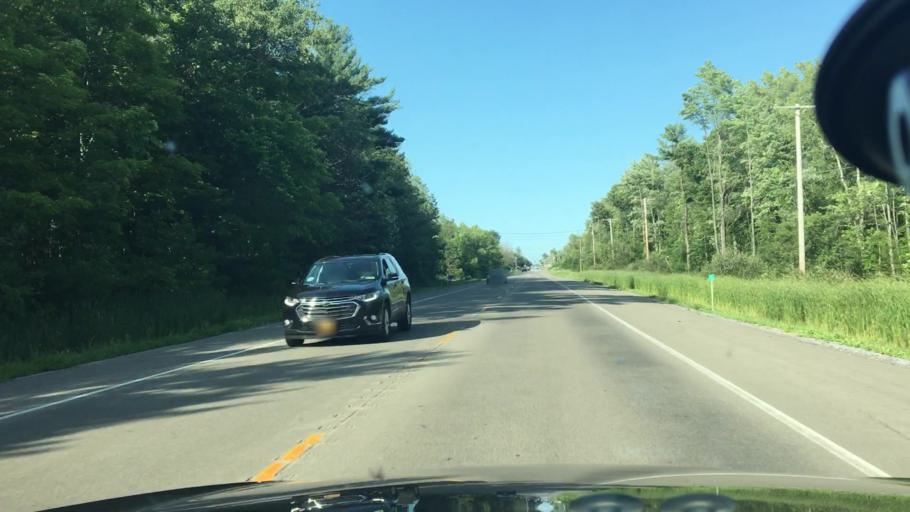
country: US
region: New York
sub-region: Erie County
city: Wanakah
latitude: 42.7029
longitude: -78.9264
